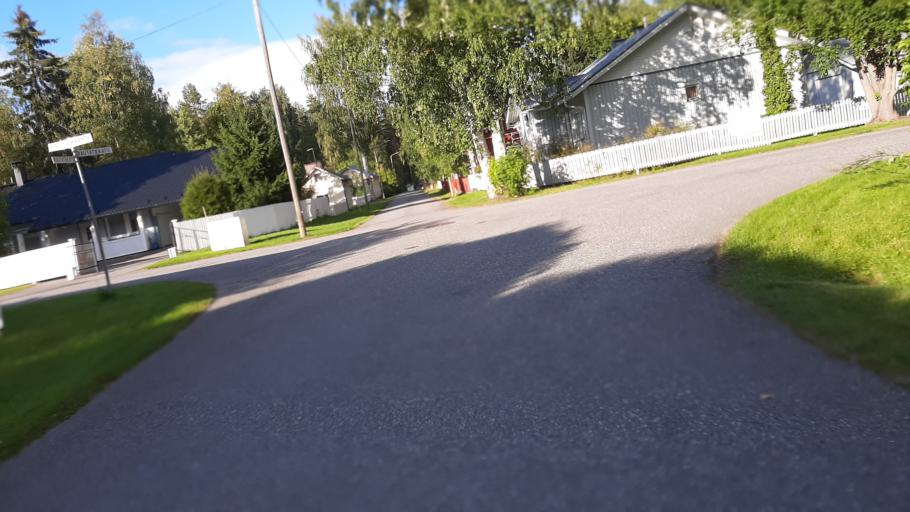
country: FI
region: North Karelia
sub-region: Joensuu
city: Joensuu
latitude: 62.6195
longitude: 29.7844
